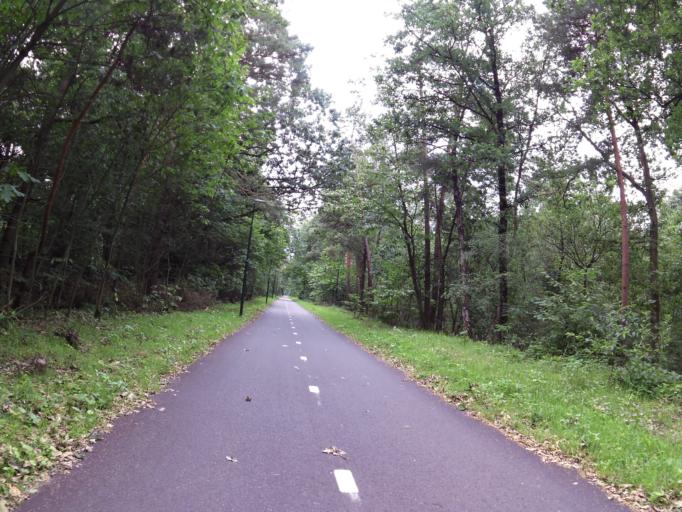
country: NL
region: North Brabant
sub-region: Gemeente Waalre
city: Waalre
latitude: 51.3755
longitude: 5.4601
